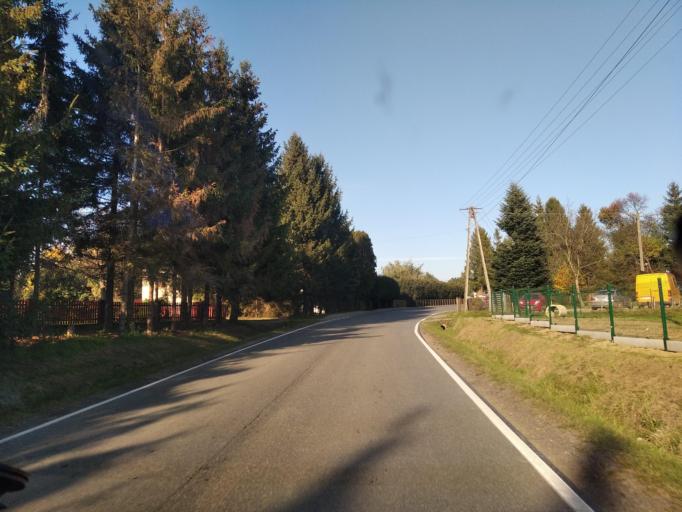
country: PL
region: Subcarpathian Voivodeship
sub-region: Powiat brzozowski
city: Turze Pole
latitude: 49.6608
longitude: 21.9998
